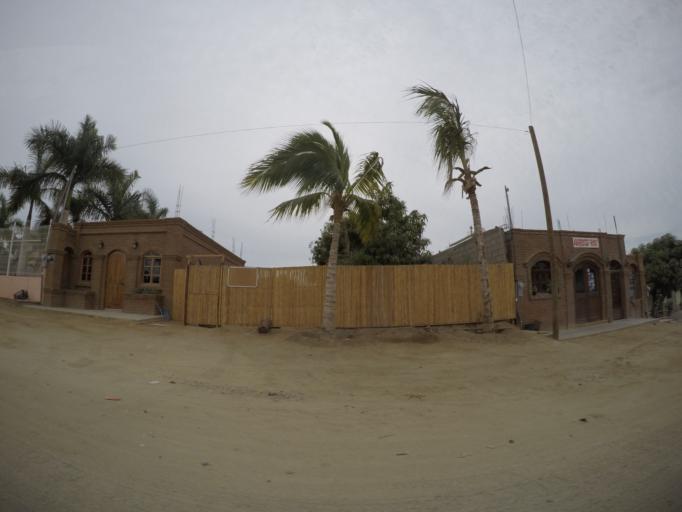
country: MX
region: Baja California Sur
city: Todos Santos
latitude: 23.4445
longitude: -110.2259
